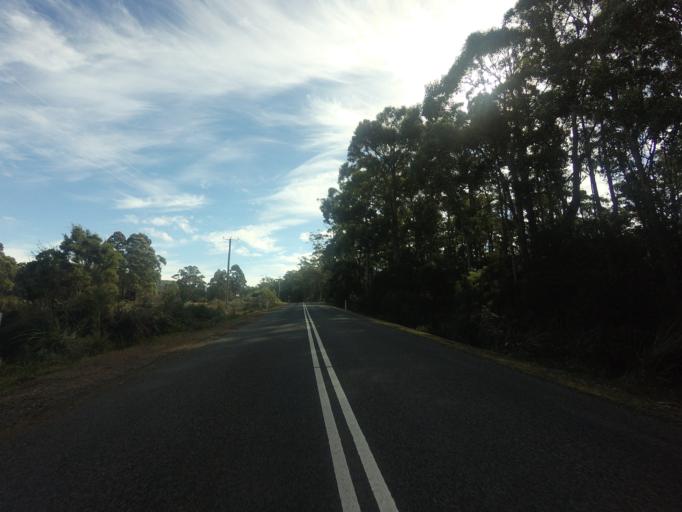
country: AU
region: Tasmania
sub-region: Clarence
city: Sandford
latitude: -43.1277
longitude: 147.7785
